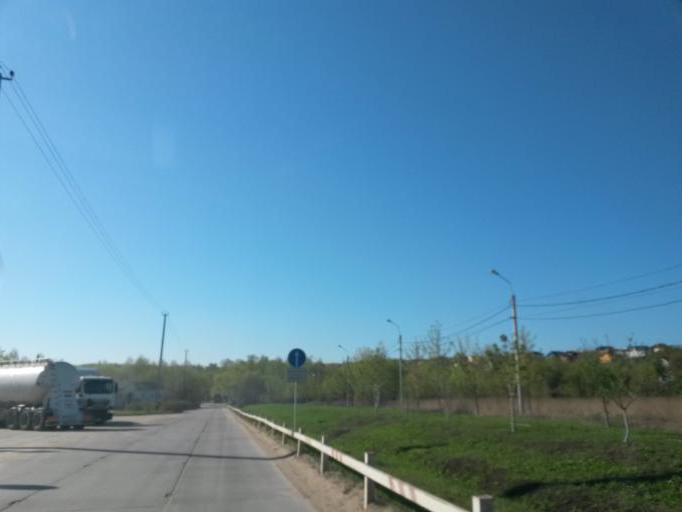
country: RU
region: Moskovskaya
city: Alekseyevka
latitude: 55.6155
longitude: 37.7934
